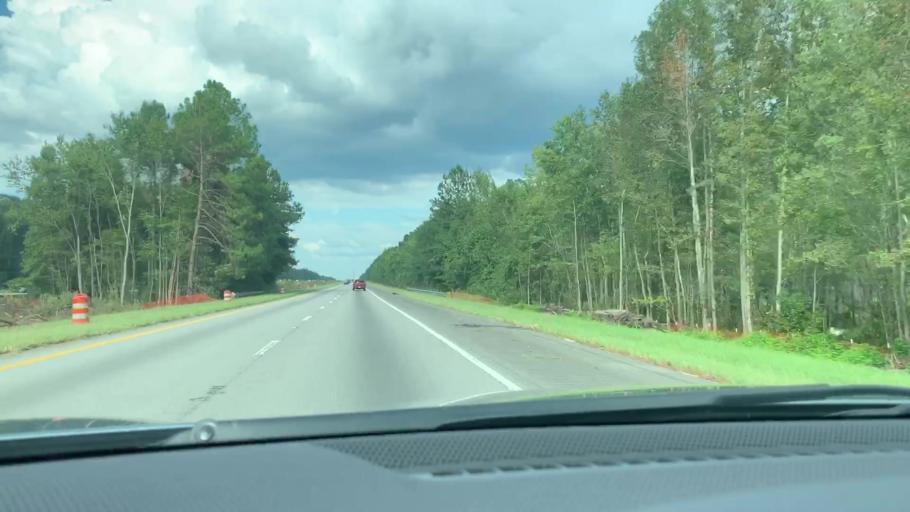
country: US
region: South Carolina
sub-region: Jasper County
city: Ridgeland
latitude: 32.5384
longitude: -80.9539
